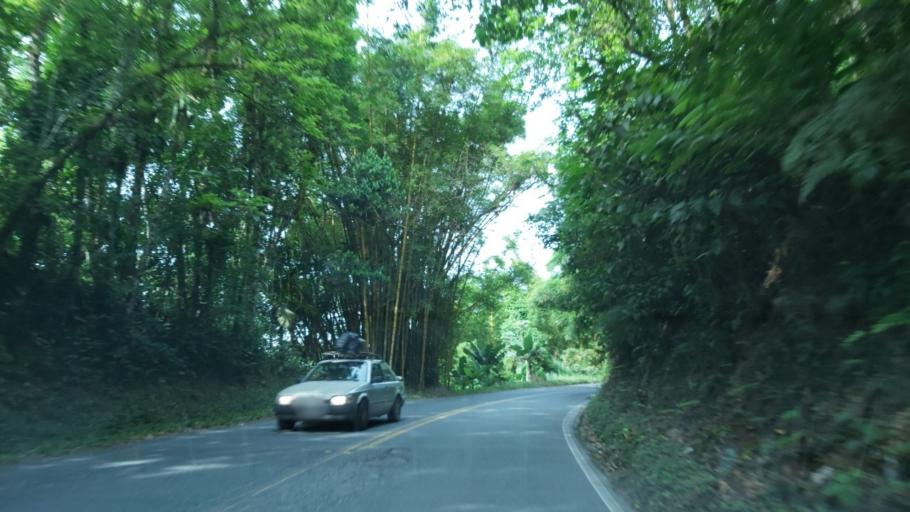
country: BR
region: Sao Paulo
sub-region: Juquia
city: Juquia
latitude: -24.1118
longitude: -47.6267
